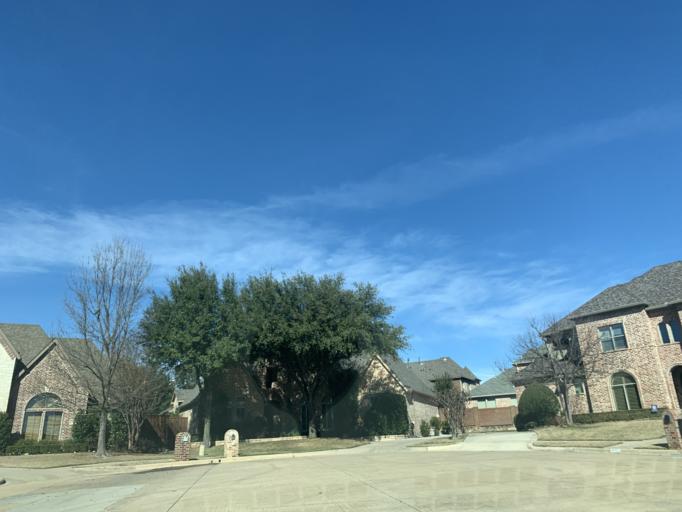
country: US
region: Texas
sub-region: Denton County
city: The Colony
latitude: 33.0708
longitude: -96.8536
